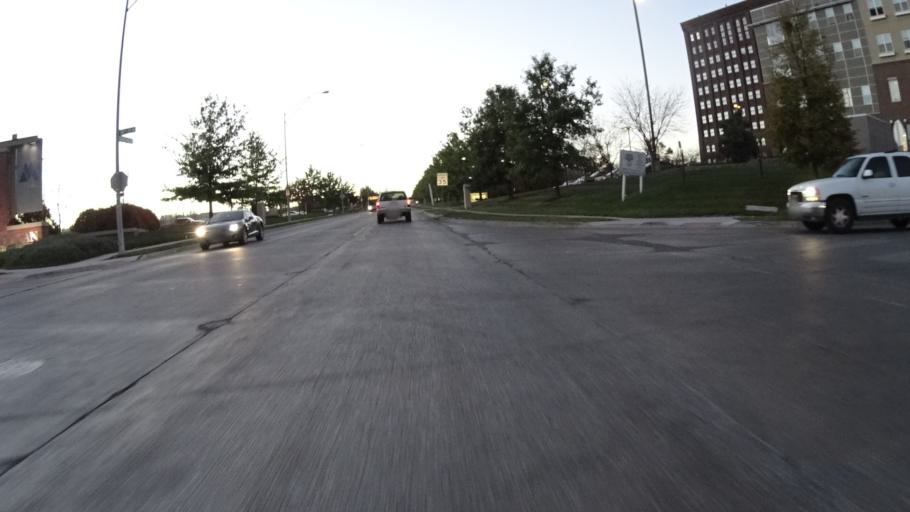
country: US
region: Nebraska
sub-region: Douglas County
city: Omaha
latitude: 41.2087
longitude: -95.9552
